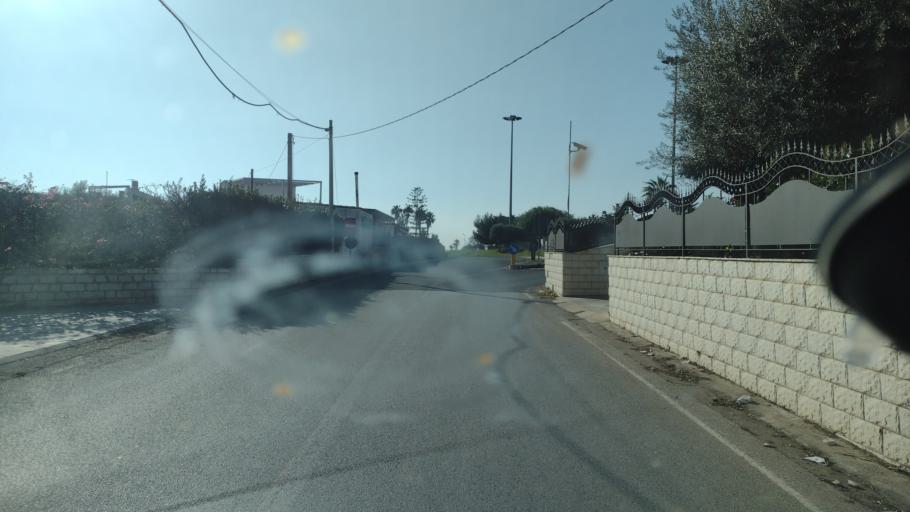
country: IT
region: Sicily
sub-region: Provincia di Siracusa
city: Avola
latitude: 36.8720
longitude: 15.1273
